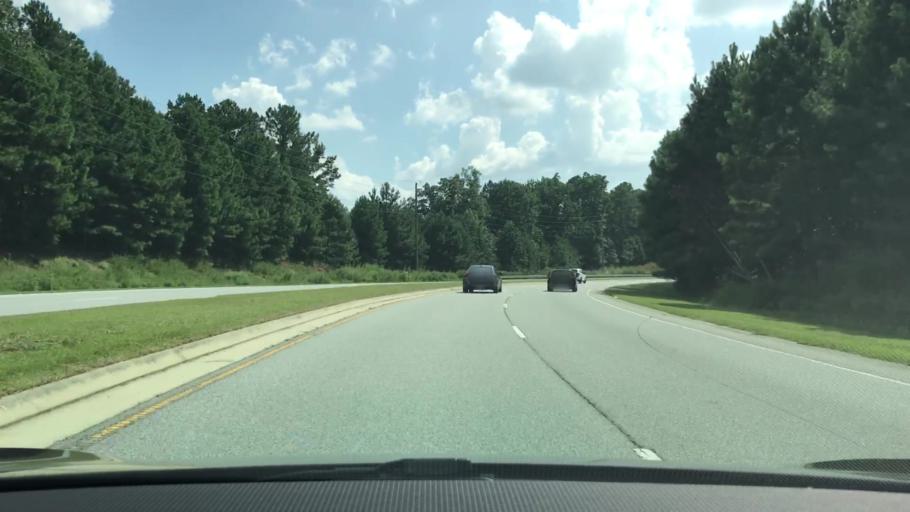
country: US
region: Georgia
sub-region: Gwinnett County
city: Sugar Hill
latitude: 34.0642
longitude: -84.0164
